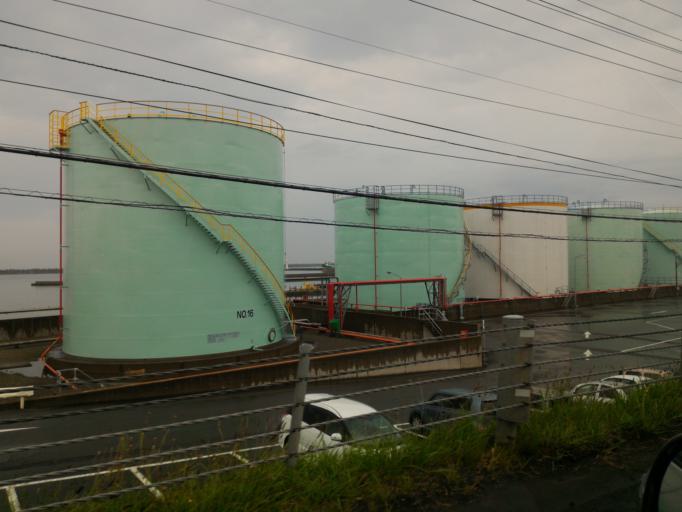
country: JP
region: Hokkaido
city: Rumoi
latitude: 43.9564
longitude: 141.6439
